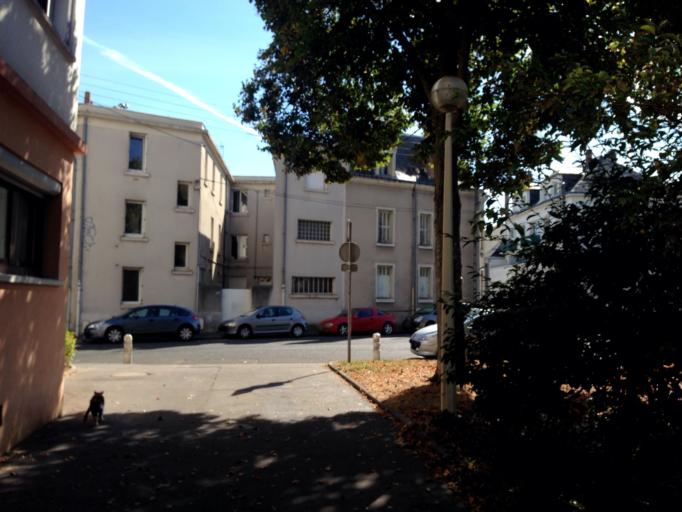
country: FR
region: Centre
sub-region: Departement d'Indre-et-Loire
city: Tours
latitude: 47.3876
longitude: 0.7003
